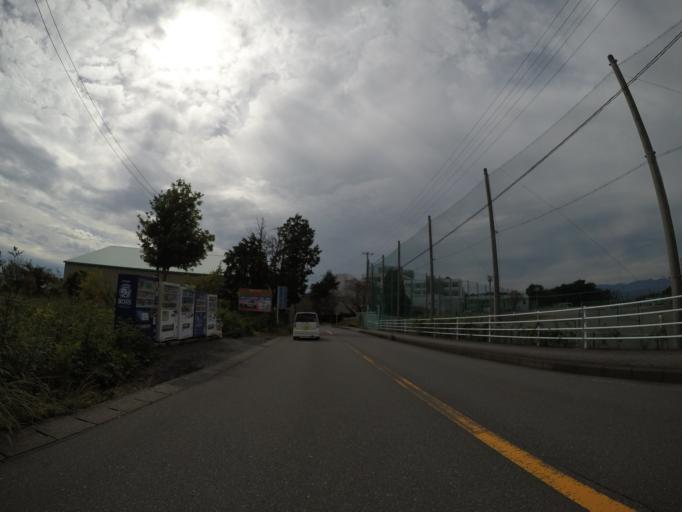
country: JP
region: Shizuoka
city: Fuji
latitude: 35.1742
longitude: 138.7212
